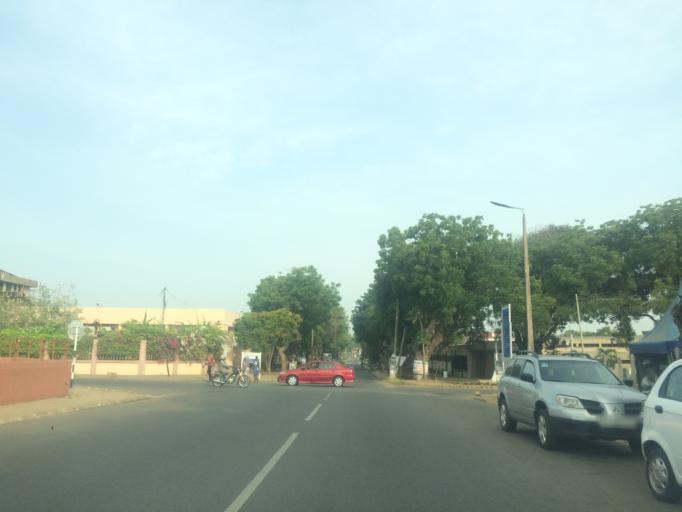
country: GH
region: Greater Accra
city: Accra
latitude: 5.5380
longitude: -0.2282
